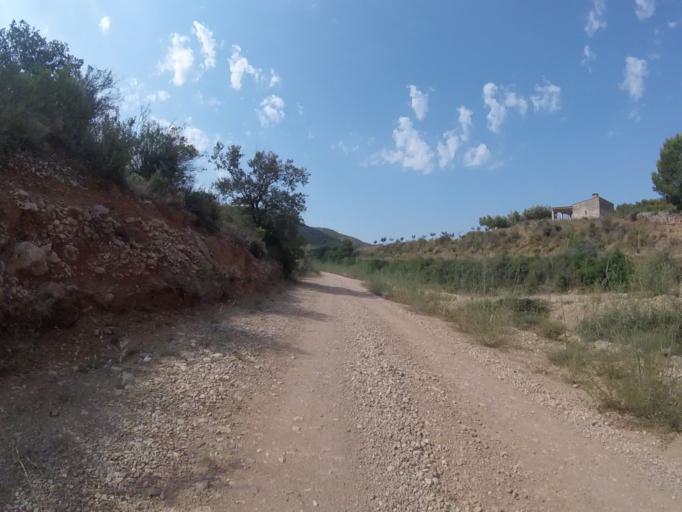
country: ES
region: Valencia
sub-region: Provincia de Castello
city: Alcala de Xivert
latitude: 40.3198
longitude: 0.1858
